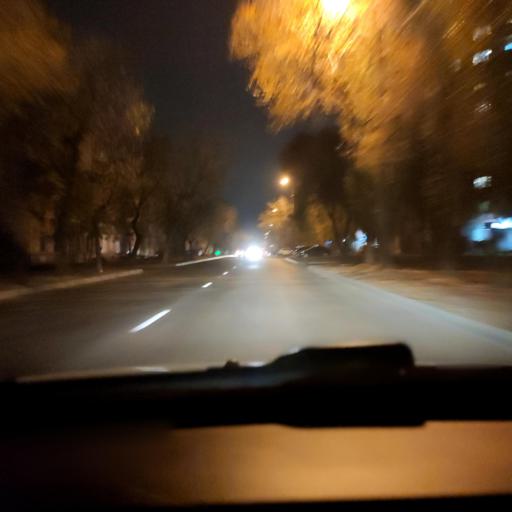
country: RU
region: Voronezj
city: Voronezh
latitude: 51.6364
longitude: 39.2380
